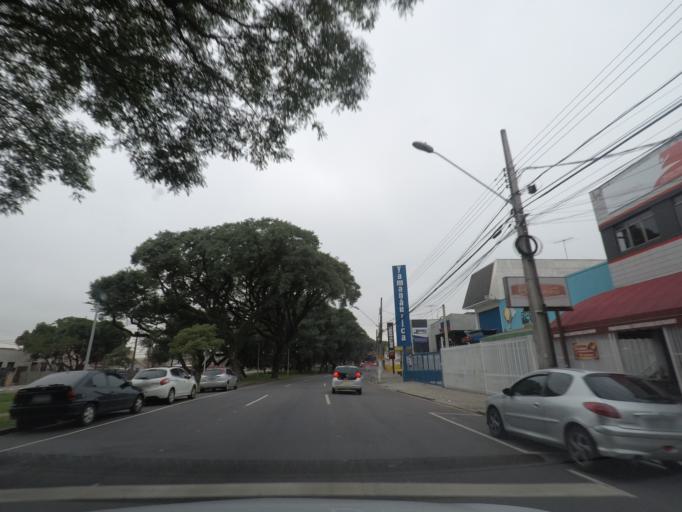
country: BR
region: Parana
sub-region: Curitiba
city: Curitiba
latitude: -25.4454
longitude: -49.2591
